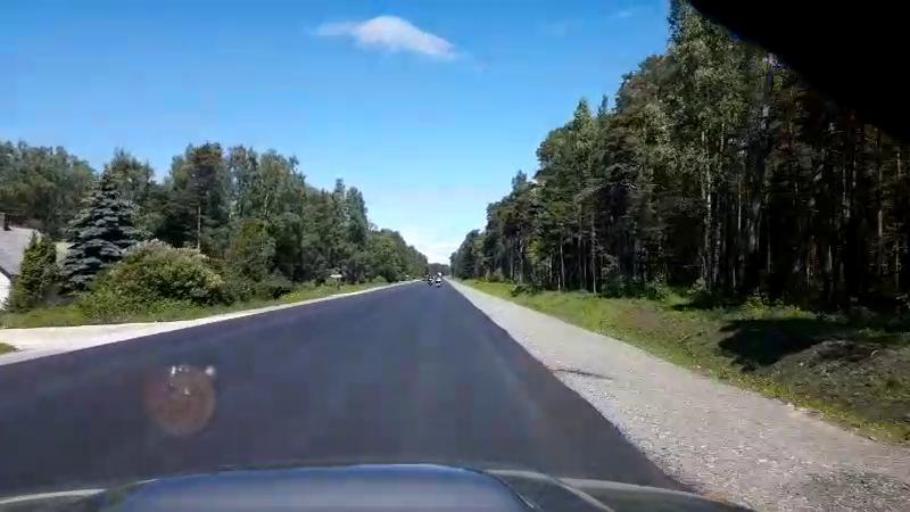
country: LV
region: Salacgrivas
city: Salacgriva
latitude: 57.8046
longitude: 24.3490
